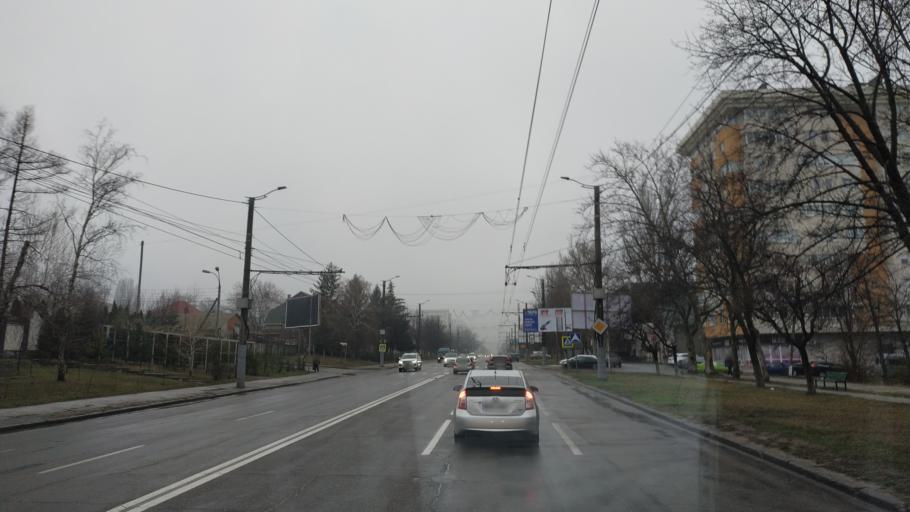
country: MD
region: Chisinau
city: Vatra
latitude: 47.0305
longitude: 28.7861
